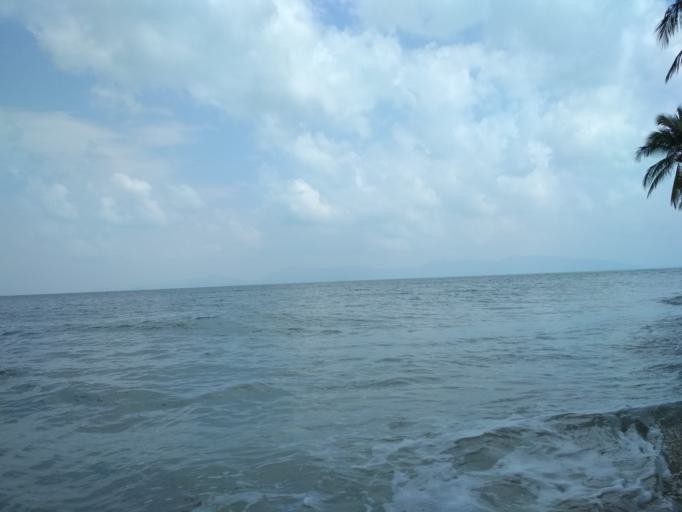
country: TH
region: Surat Thani
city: Ko Samui
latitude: 9.5828
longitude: 99.9668
